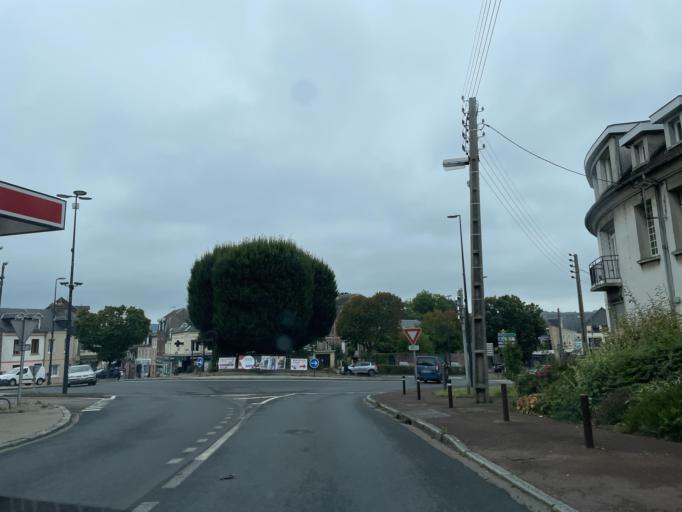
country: FR
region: Haute-Normandie
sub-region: Departement de la Seine-Maritime
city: Eu
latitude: 50.0431
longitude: 1.4195
